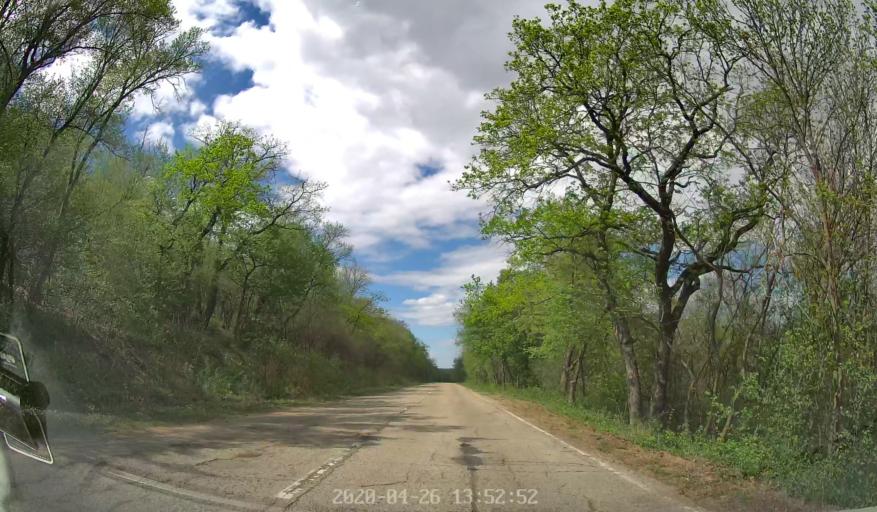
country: MD
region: Telenesti
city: Cocieri
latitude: 47.2750
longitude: 29.1148
